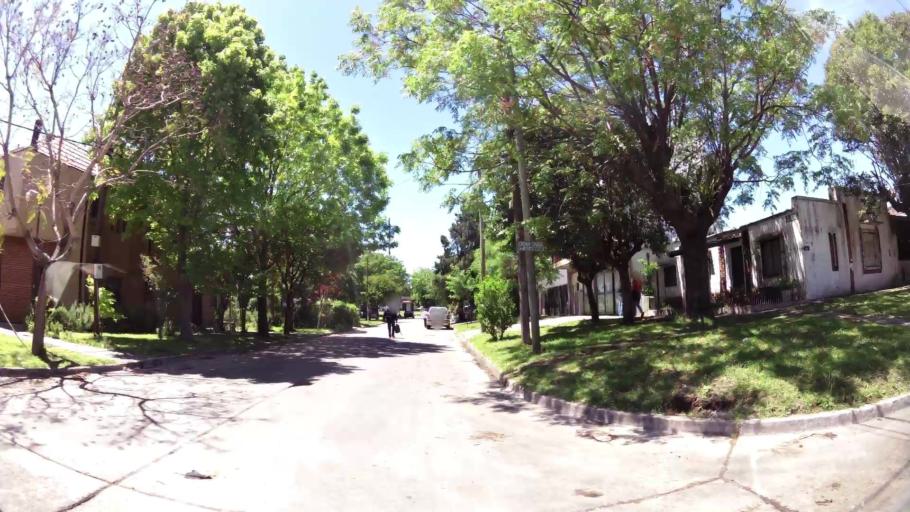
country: AR
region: Buenos Aires
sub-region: Partido de Quilmes
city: Quilmes
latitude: -34.7365
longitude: -58.2847
